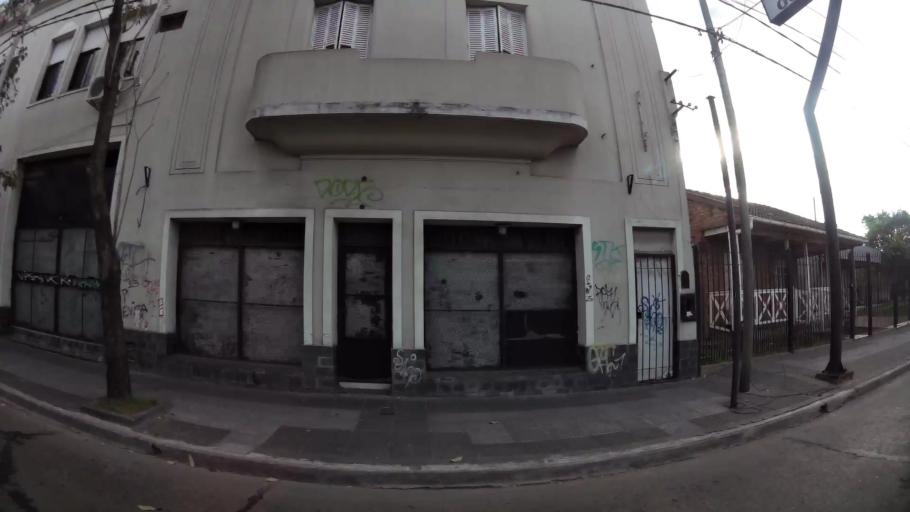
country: AR
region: Buenos Aires
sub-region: Partido de Avellaneda
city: Avellaneda
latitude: -34.6837
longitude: -58.3476
